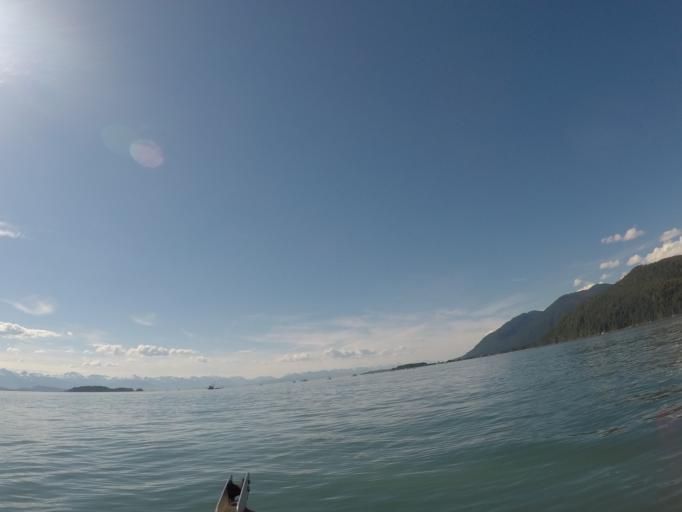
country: US
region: Alaska
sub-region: Juneau City and Borough
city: Juneau
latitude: 58.4936
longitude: -134.8140
